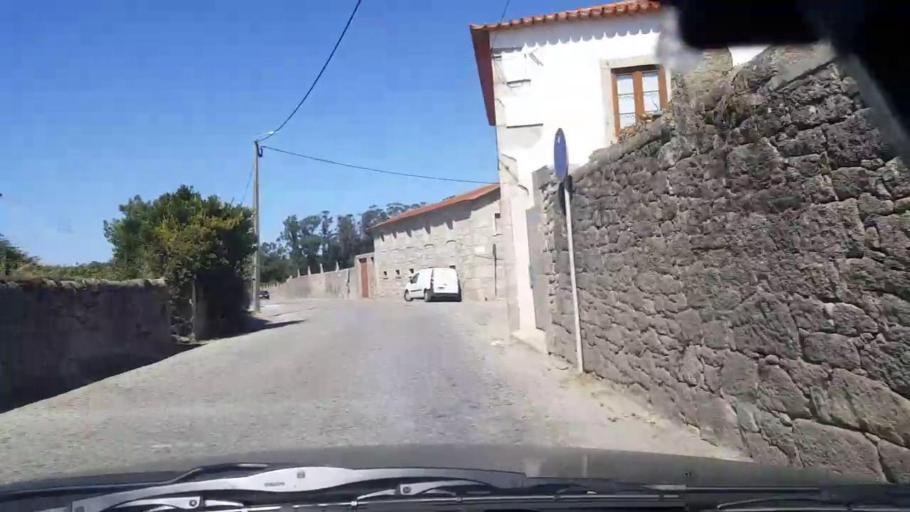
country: PT
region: Porto
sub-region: Vila do Conde
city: Arvore
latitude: 41.3264
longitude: -8.7054
